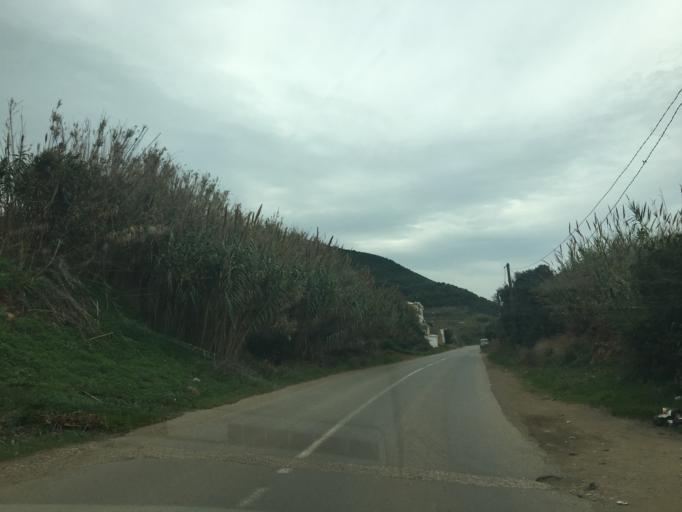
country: DZ
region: Tipaza
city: Tipasa
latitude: 36.6334
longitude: 2.3004
